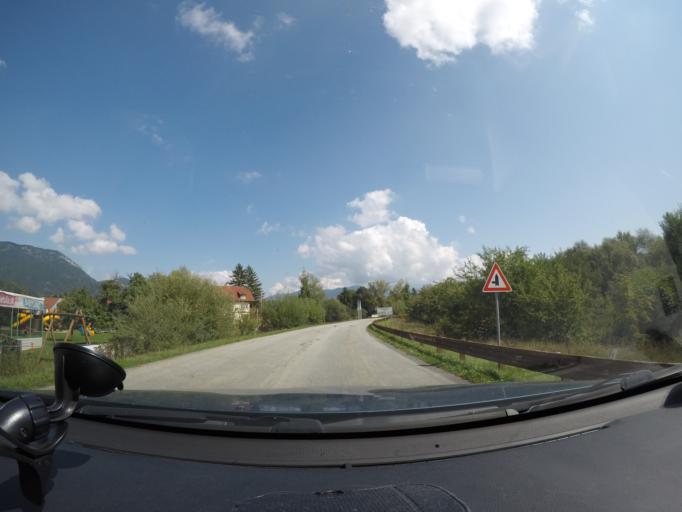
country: SK
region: Zilinsky
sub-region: Okres Liptovsky Mikulas
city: Liptovsky Mikulas
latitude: 49.1353
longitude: 19.5113
